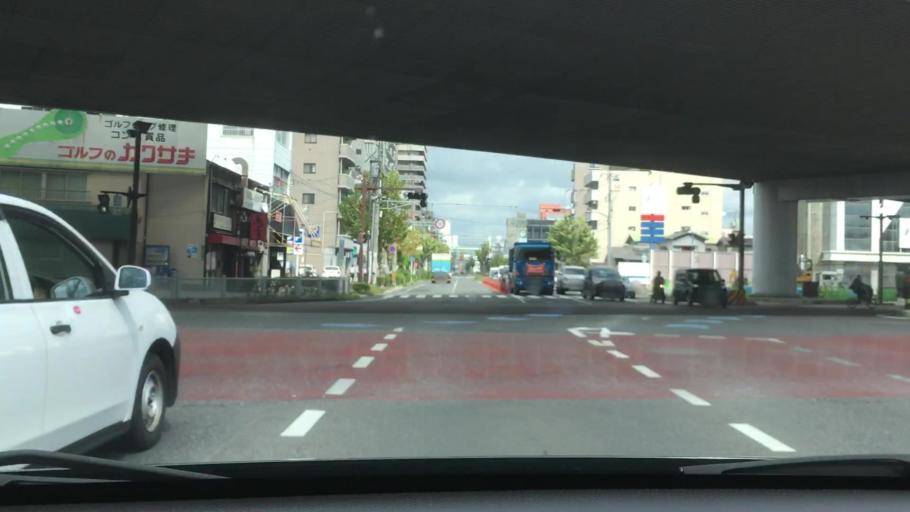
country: JP
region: Hiroshima
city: Hiroshima-shi
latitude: 34.3872
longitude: 132.4316
